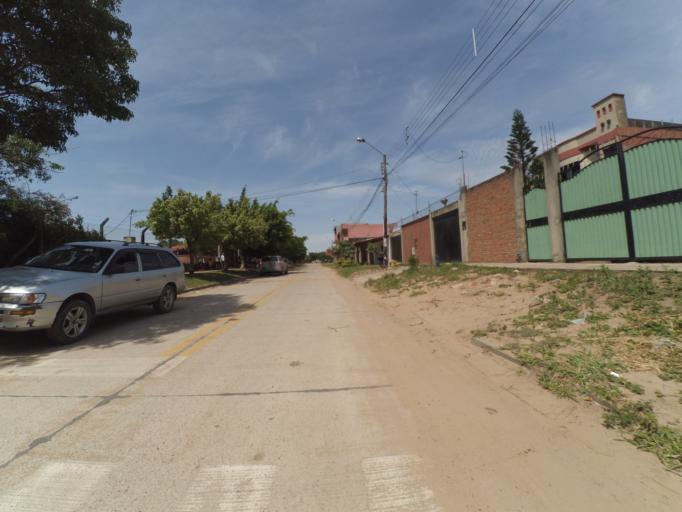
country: BO
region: Santa Cruz
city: Santa Cruz de la Sierra
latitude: -17.8308
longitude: -63.2345
